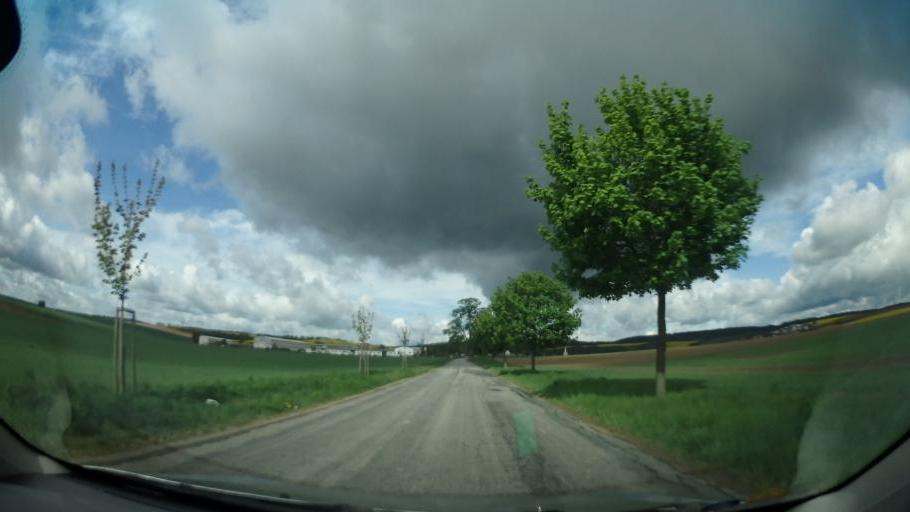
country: CZ
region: South Moravian
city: Ricany
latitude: 49.2285
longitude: 16.4148
